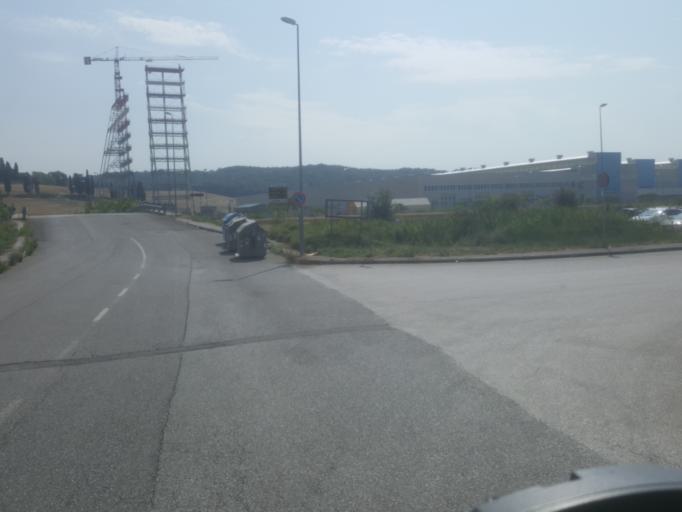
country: IT
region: Tuscany
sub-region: Provincia di Livorno
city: Guasticce
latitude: 43.5960
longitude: 10.4005
